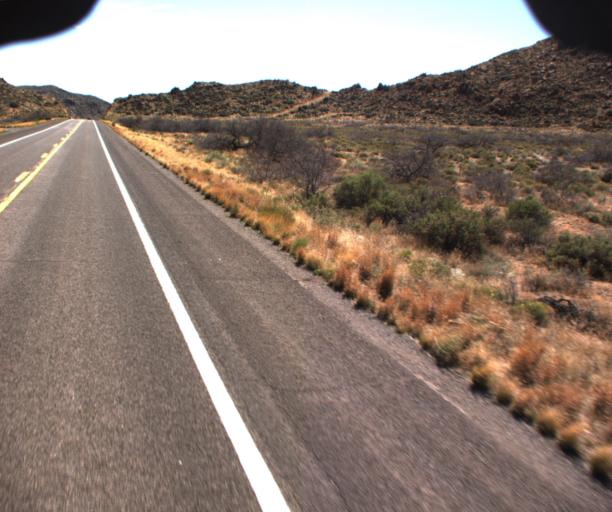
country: US
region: Arizona
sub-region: Mohave County
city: Peach Springs
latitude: 35.3745
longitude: -113.6679
